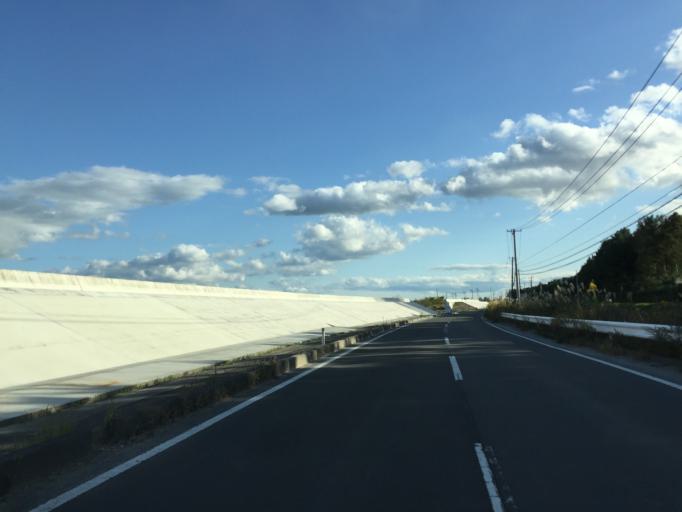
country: JP
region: Miyagi
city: Marumori
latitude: 37.8440
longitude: 140.9492
